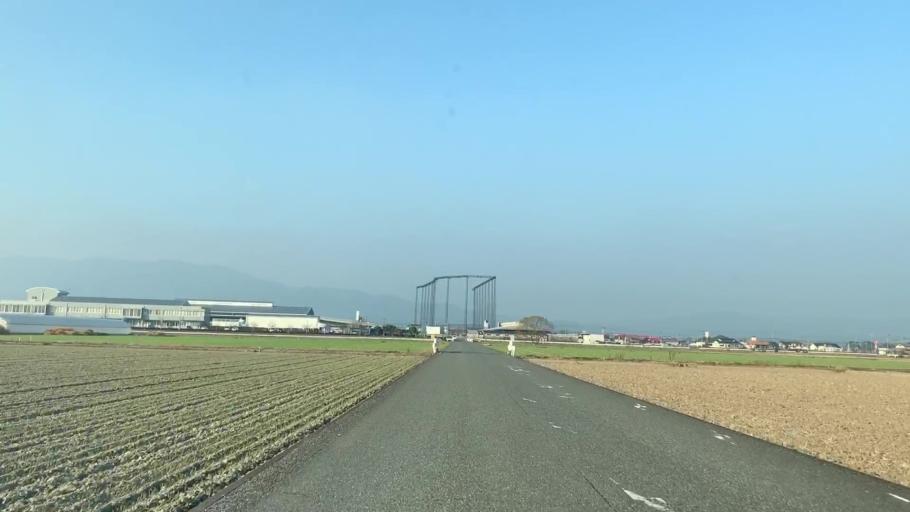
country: JP
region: Saga Prefecture
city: Saga-shi
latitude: 33.2604
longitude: 130.2482
